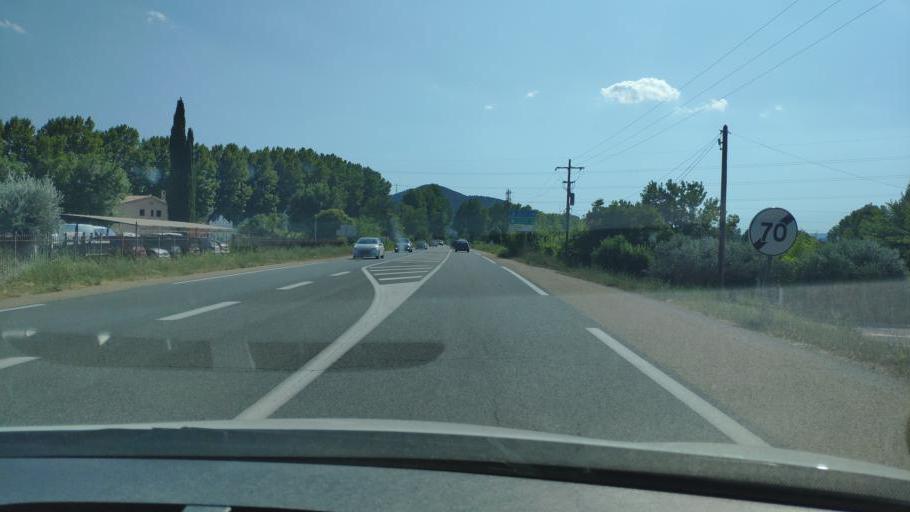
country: FR
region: Provence-Alpes-Cote d'Azur
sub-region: Departement du Var
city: Les Arcs
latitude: 43.4457
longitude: 6.4700
